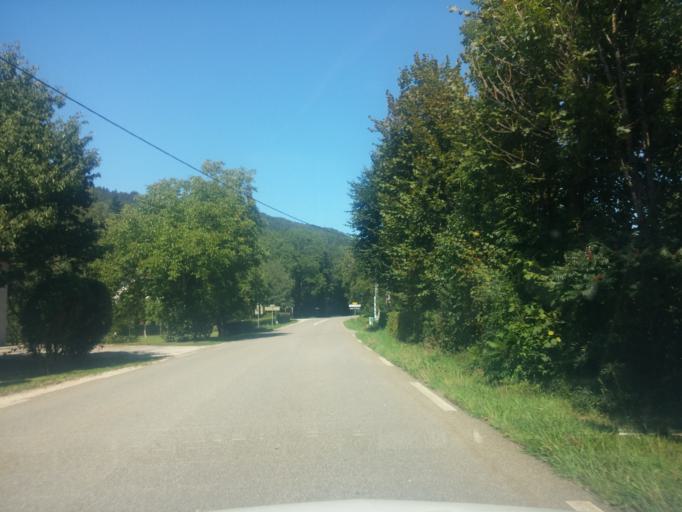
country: FR
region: Franche-Comte
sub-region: Departement du Jura
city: Saint-Lupicin
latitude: 46.4109
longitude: 5.7951
